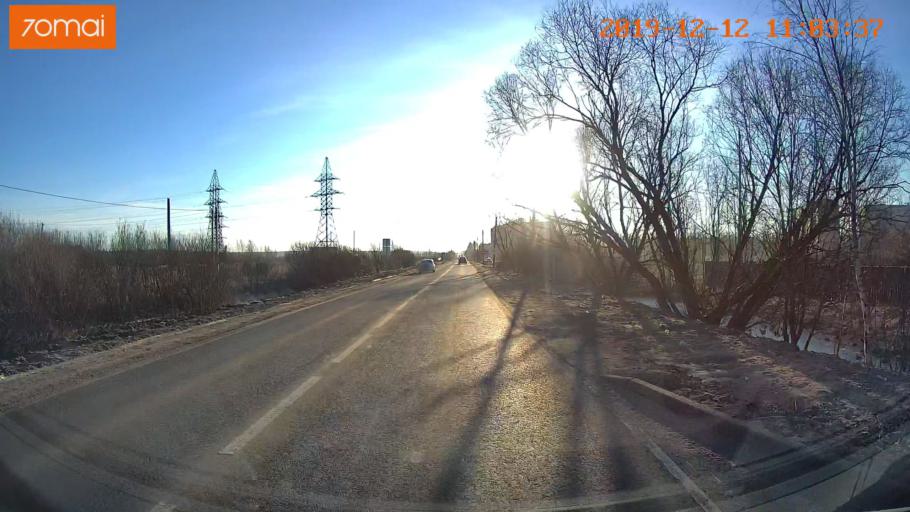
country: RU
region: Ivanovo
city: Kokhma
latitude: 56.9574
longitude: 41.1018
